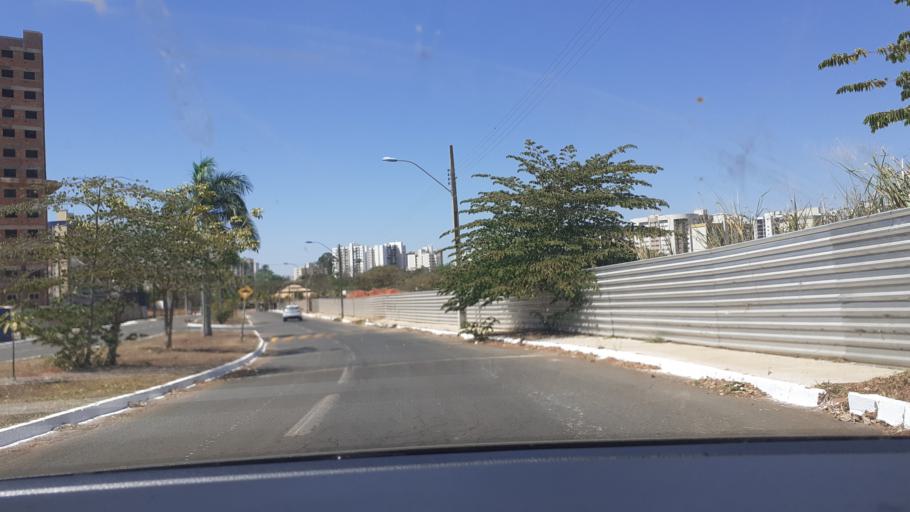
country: BR
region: Goias
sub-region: Caldas Novas
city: Caldas Novas
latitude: -17.7415
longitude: -48.6357
